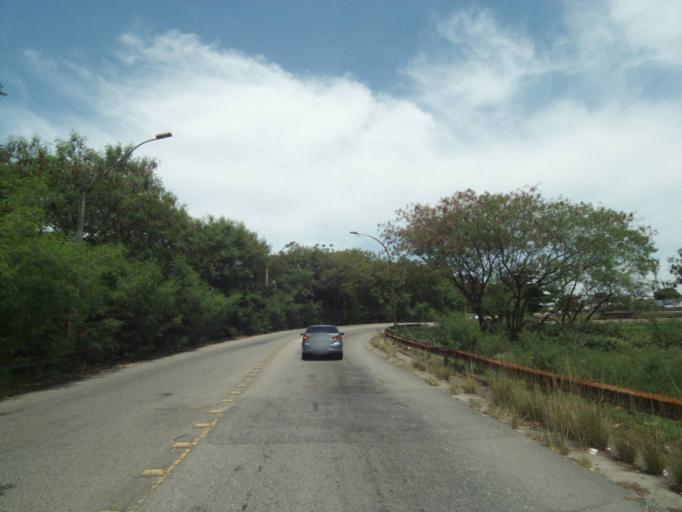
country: BR
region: Rio de Janeiro
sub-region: Duque De Caxias
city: Duque de Caxias
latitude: -22.7992
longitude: -43.3093
